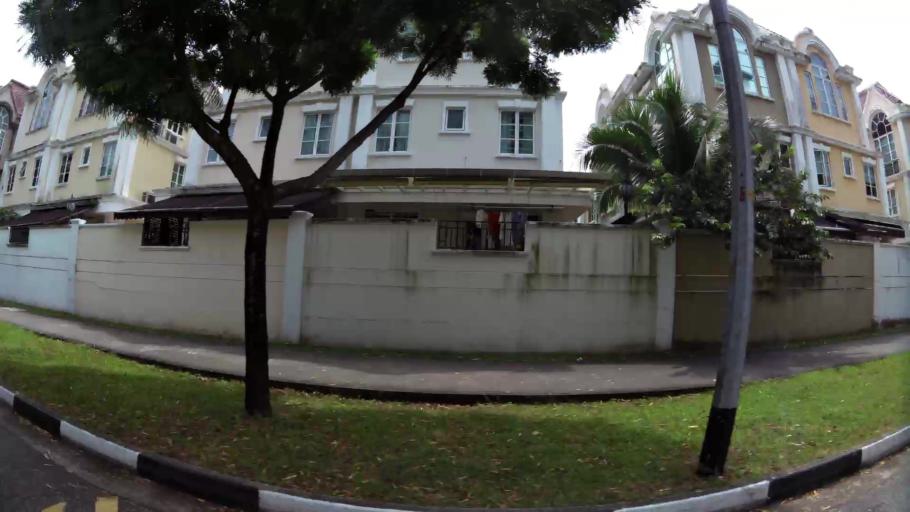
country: SG
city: Singapore
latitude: 1.3406
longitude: 103.7607
